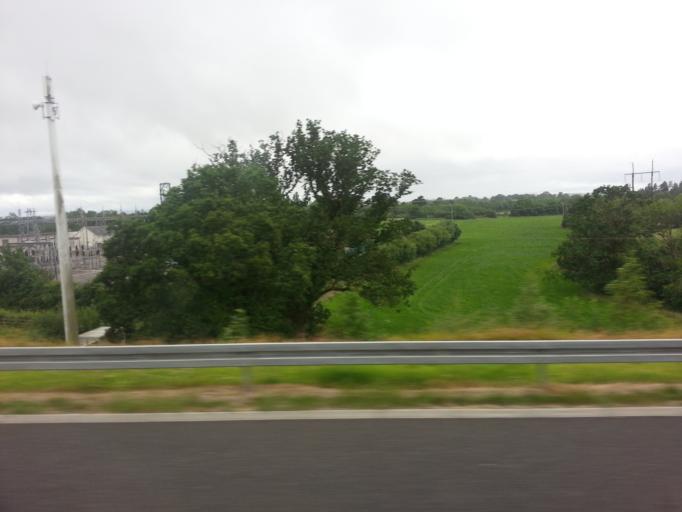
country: IE
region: Leinster
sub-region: Kilkenny
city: Kilkenny
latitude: 52.6419
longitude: -7.1711
